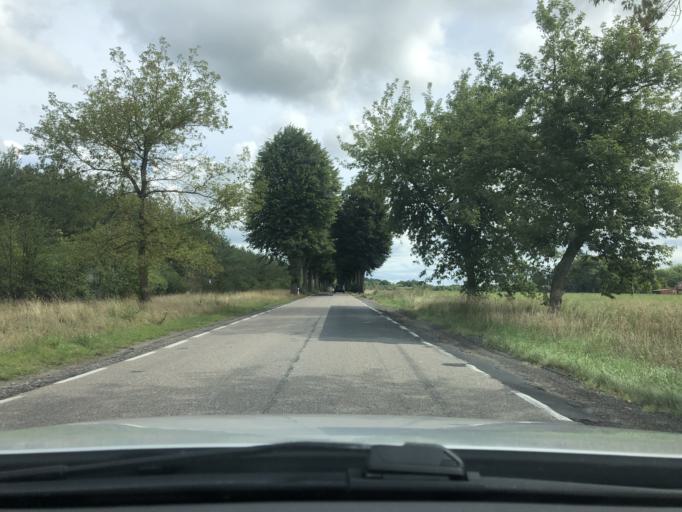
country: PL
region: Greater Poland Voivodeship
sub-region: Powiat czarnkowsko-trzcianecki
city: Wielen
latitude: 52.9036
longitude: 16.1454
